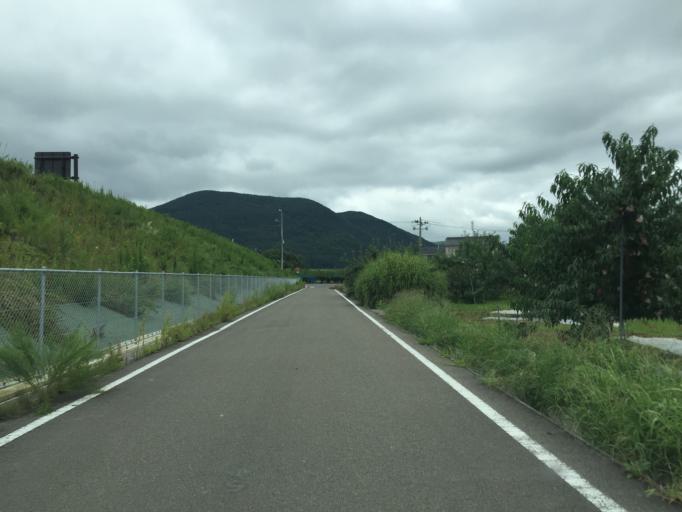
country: JP
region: Fukushima
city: Fukushima-shi
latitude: 37.7964
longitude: 140.4132
